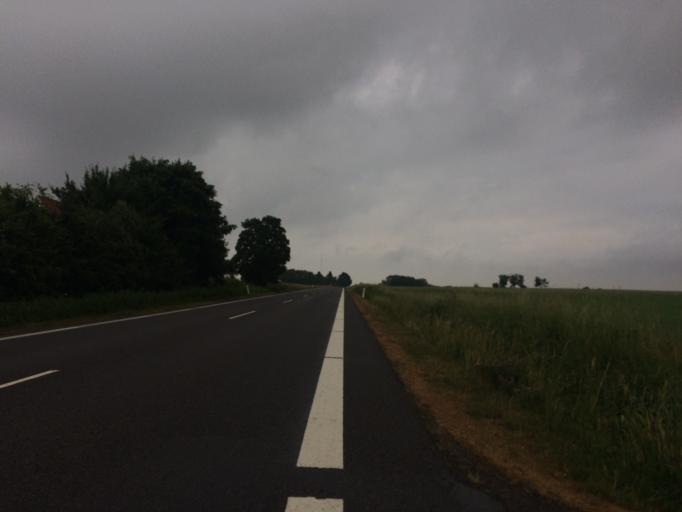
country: DK
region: Capital Region
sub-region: Bornholm Kommune
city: Akirkeby
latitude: 55.1363
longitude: 14.8449
